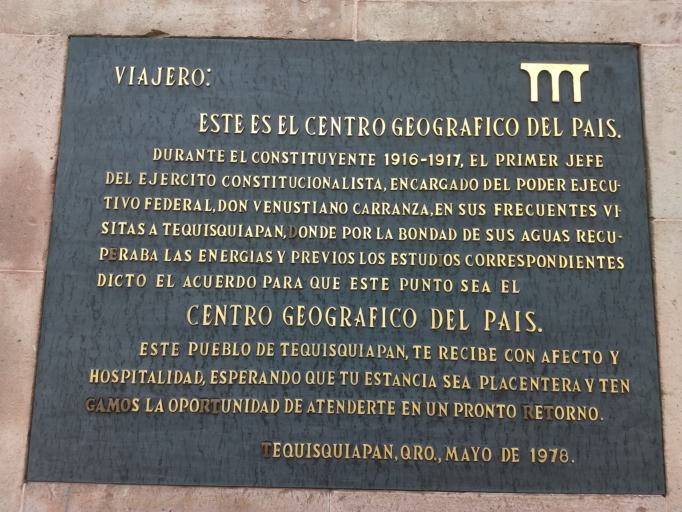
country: MX
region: Queretaro
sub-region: Tequisquiapan
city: Tequisquiapan
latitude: 20.5216
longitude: -99.8940
